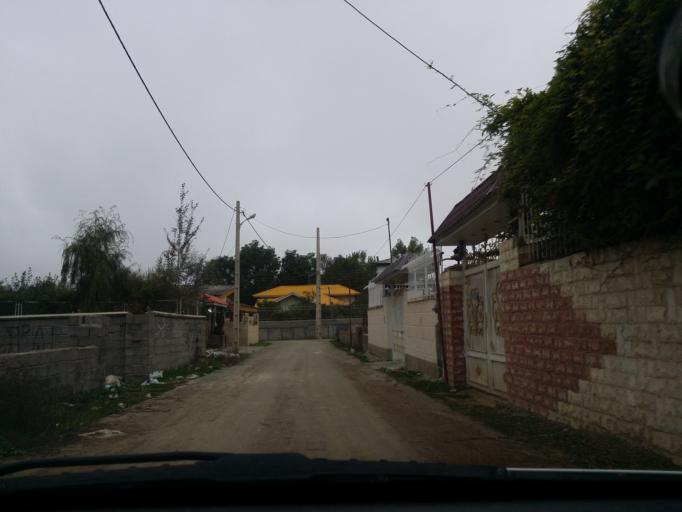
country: IR
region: Mazandaran
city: Chalus
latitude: 36.5088
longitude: 51.2310
